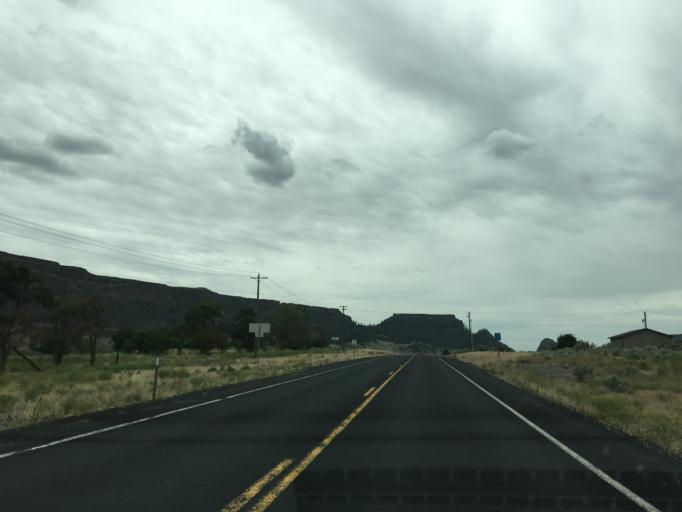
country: US
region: Washington
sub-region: Okanogan County
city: Coulee Dam
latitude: 47.9052
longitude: -119.0648
